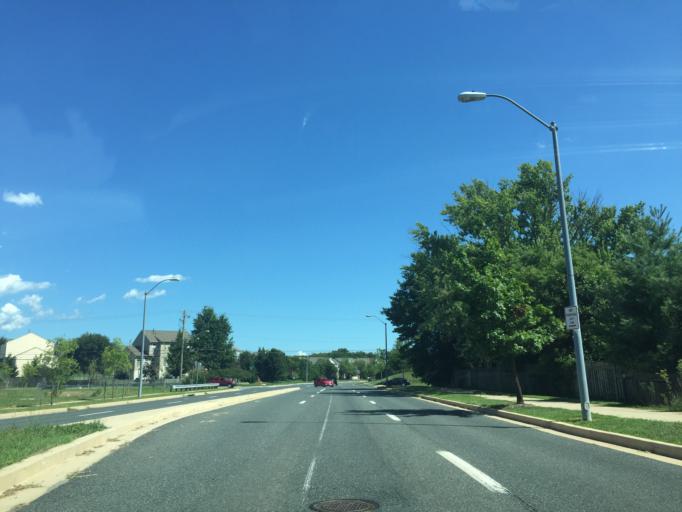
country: US
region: Maryland
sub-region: Baltimore County
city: Perry Hall
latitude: 39.4123
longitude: -76.4487
